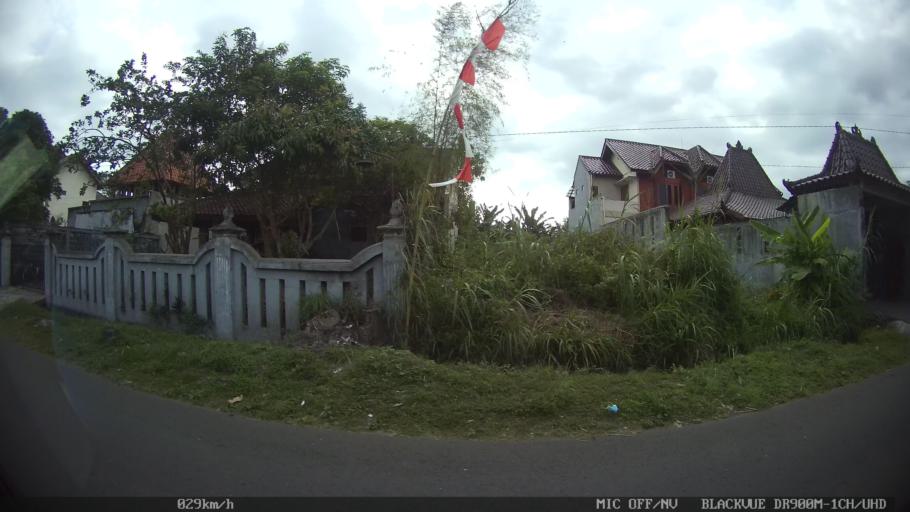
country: ID
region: Daerah Istimewa Yogyakarta
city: Sleman
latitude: -7.6852
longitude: 110.4237
